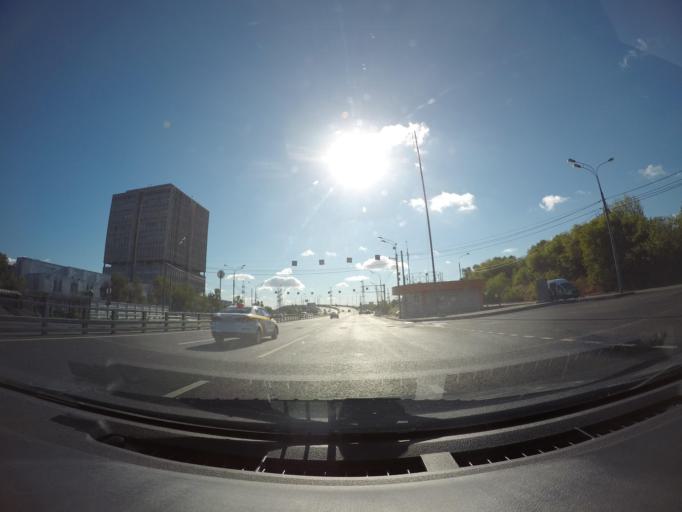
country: RU
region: Moscow
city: Veshnyaki
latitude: 55.7136
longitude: 37.8288
